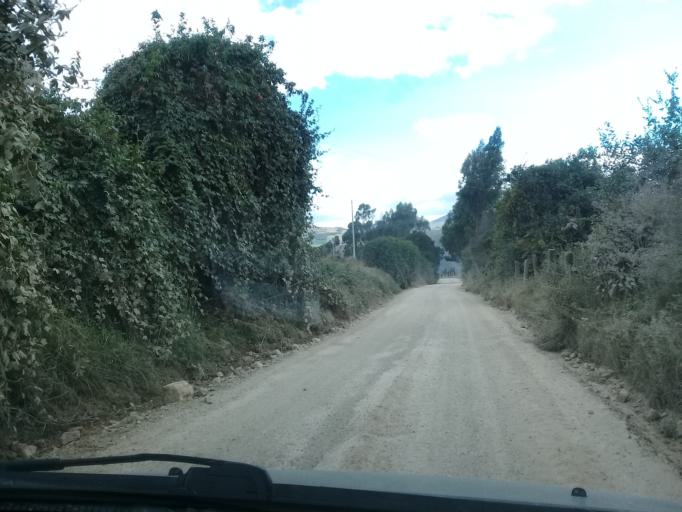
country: CO
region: Cundinamarca
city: Lenguazaque
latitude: 5.2861
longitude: -73.6733
